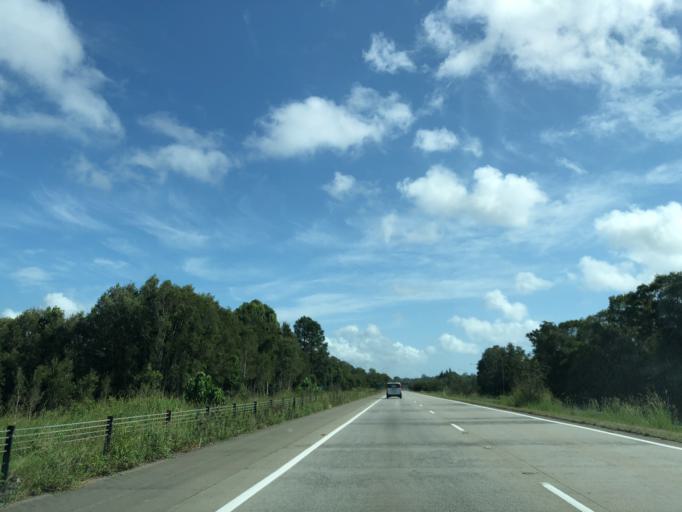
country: AU
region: New South Wales
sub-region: Byron Shire
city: Brunswick Heads
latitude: -28.5907
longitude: 153.5445
